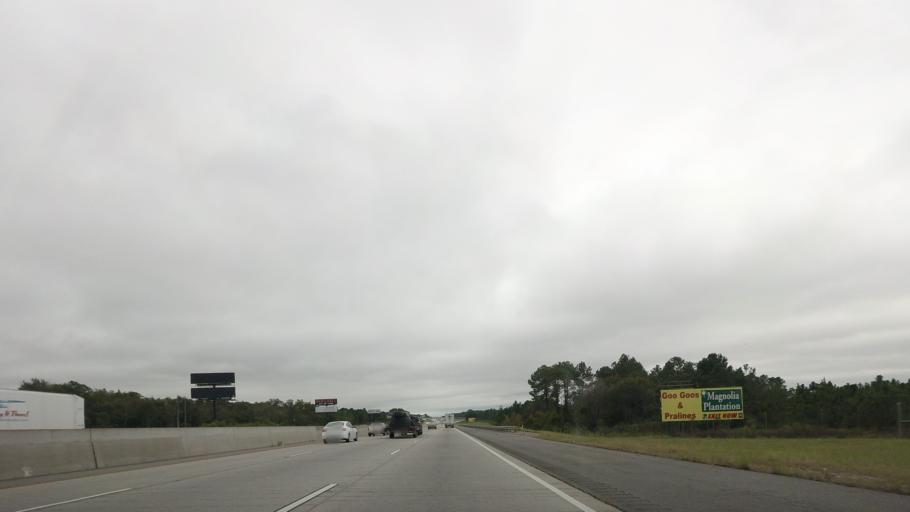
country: US
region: Georgia
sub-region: Tift County
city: Unionville
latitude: 31.3713
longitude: -83.4935
